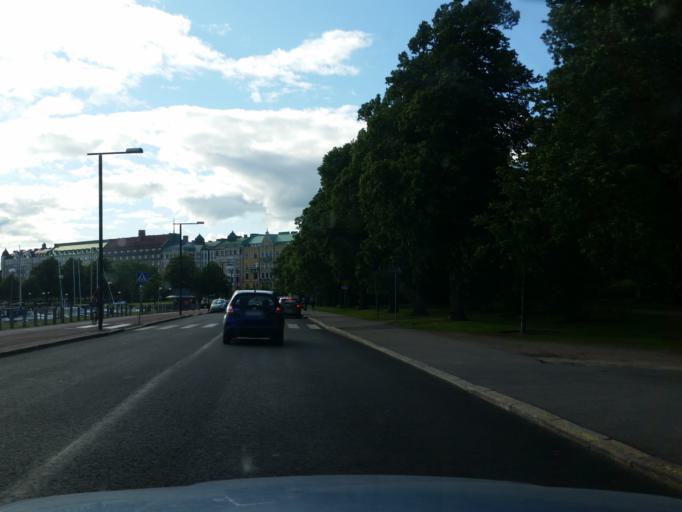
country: FI
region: Uusimaa
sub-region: Helsinki
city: Helsinki
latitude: 60.1546
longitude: 24.9539
